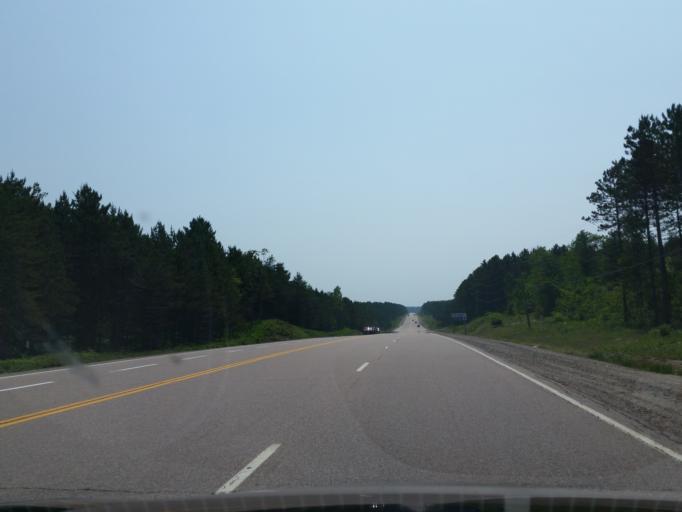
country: CA
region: Ontario
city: Deep River
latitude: 46.1816
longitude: -77.8480
